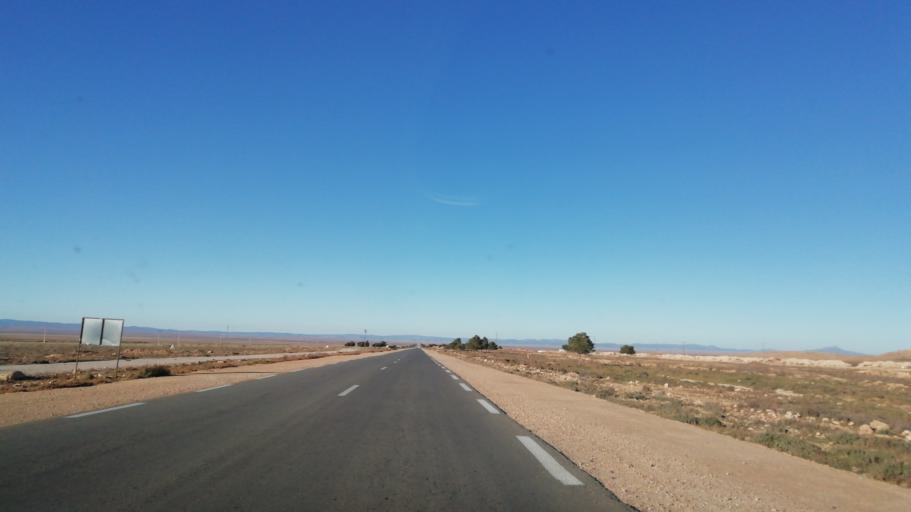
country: DZ
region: Tlemcen
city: Sebdou
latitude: 34.3030
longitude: -1.2615
